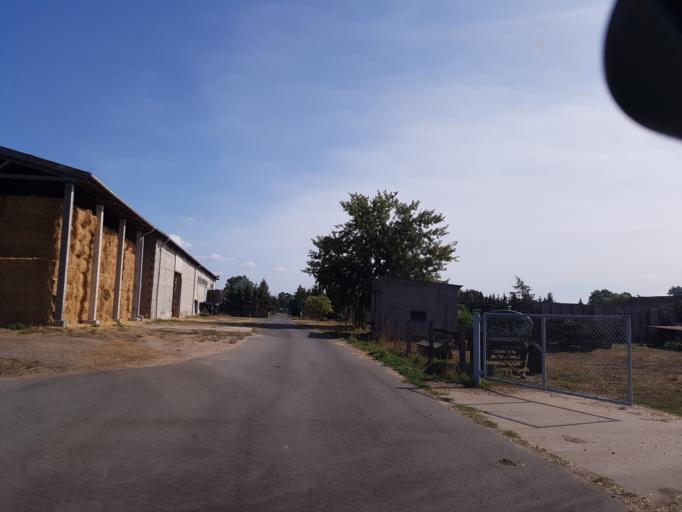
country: DE
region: Brandenburg
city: Sonnewalde
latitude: 51.6679
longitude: 13.6383
